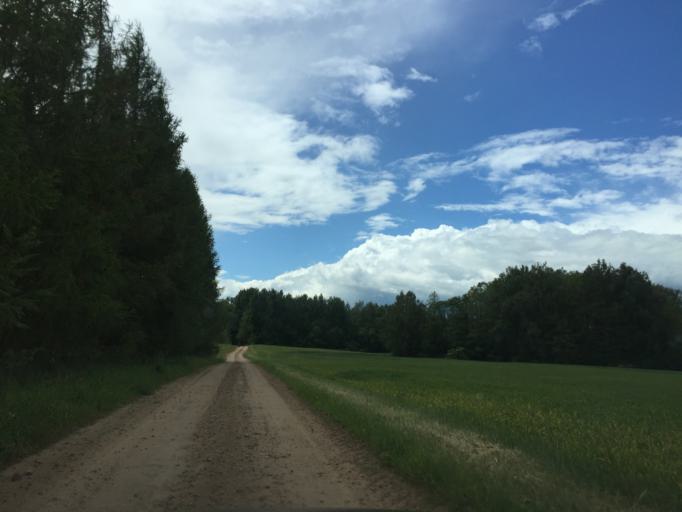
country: LV
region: Lecava
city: Iecava
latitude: 56.5567
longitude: 24.1587
